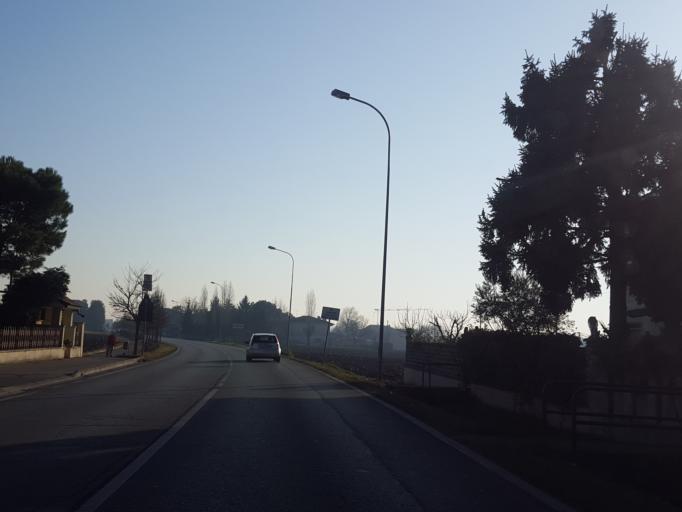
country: IT
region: Veneto
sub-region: Provincia di Vicenza
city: Marola
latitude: 45.5310
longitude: 11.6307
